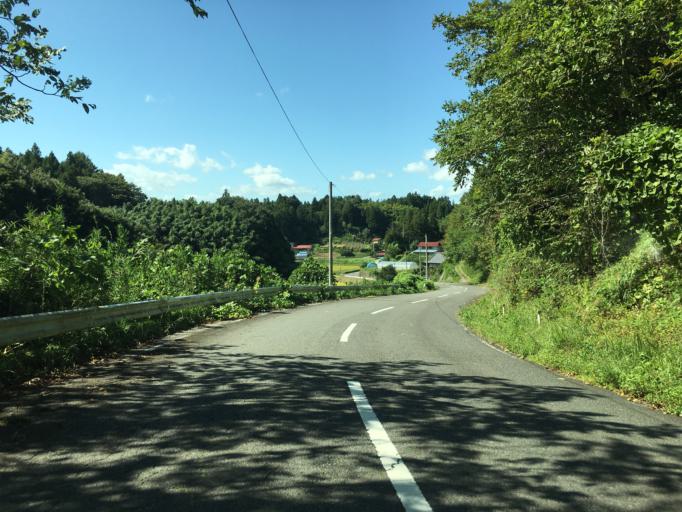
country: JP
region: Fukushima
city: Sukagawa
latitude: 37.2781
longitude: 140.4638
